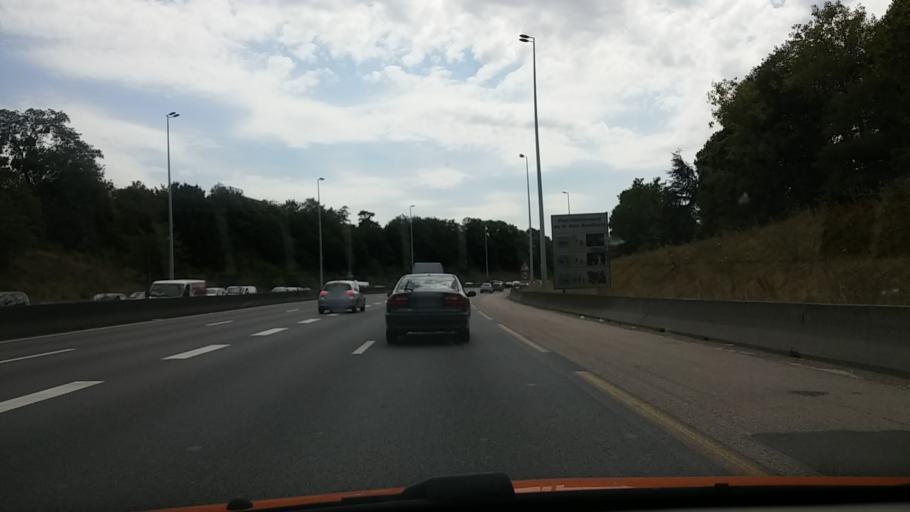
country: FR
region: Ile-de-France
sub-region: Departement du Val-de-Marne
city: Joinville-le-Pont
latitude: 48.8230
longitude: 2.4626
